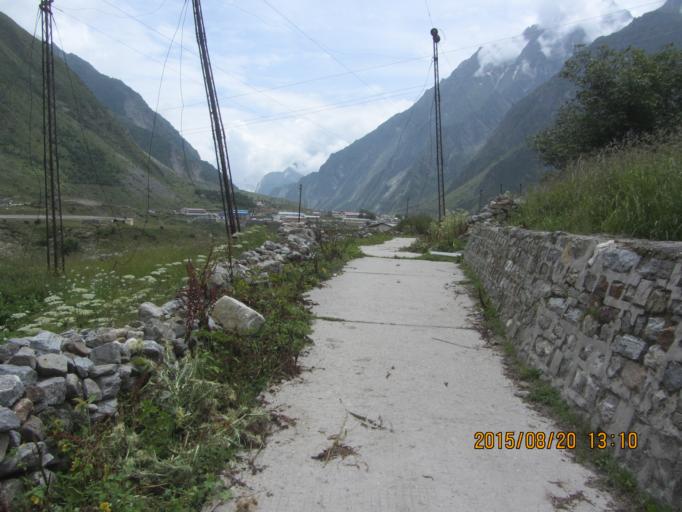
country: IN
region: Uttarakhand
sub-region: Chamoli
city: Joshimath
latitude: 30.7537
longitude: 79.4956
